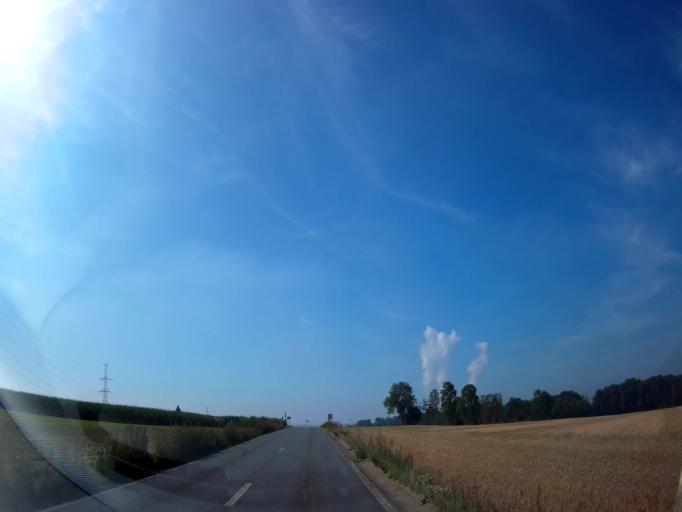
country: BE
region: Wallonia
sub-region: Province de Liege
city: Verlaine
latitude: 50.5814
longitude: 5.3334
